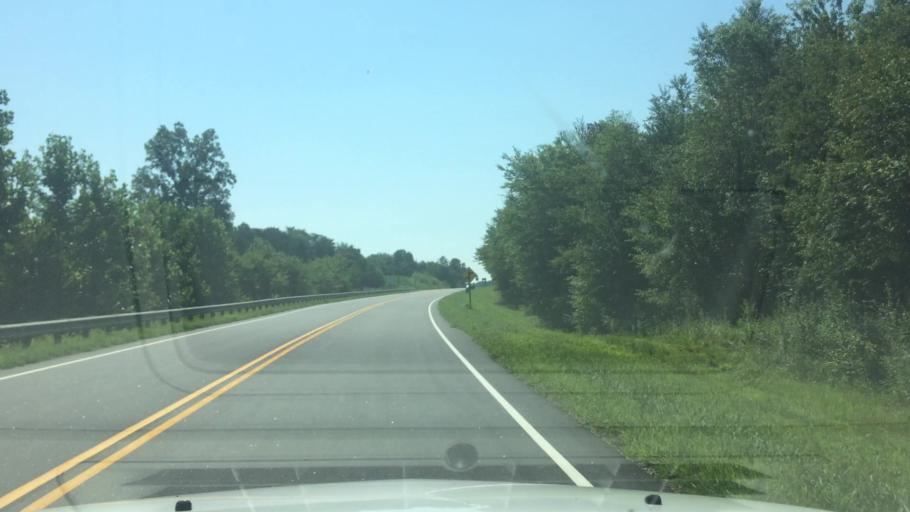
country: US
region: North Carolina
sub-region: Alexander County
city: Taylorsville
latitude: 35.9245
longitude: -81.2643
